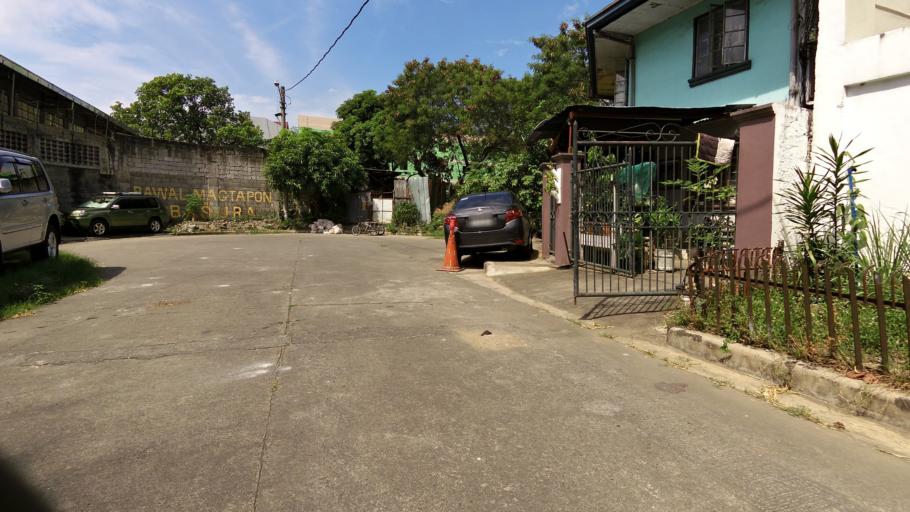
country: PH
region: Calabarzon
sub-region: Province of Rizal
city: Cainta
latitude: 14.5759
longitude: 121.0946
